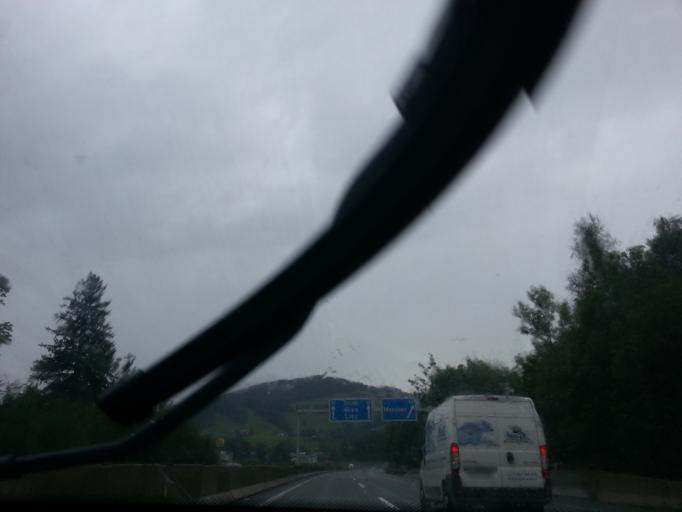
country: AT
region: Upper Austria
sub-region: Politischer Bezirk Vocklabruck
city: Mondsee
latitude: 47.8579
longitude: 13.3332
